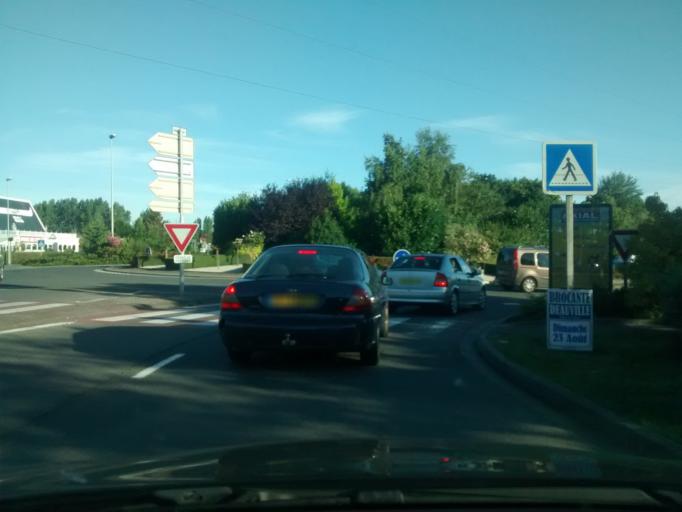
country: FR
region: Lower Normandy
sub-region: Departement du Calvados
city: Touques
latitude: 49.3469
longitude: 0.0977
